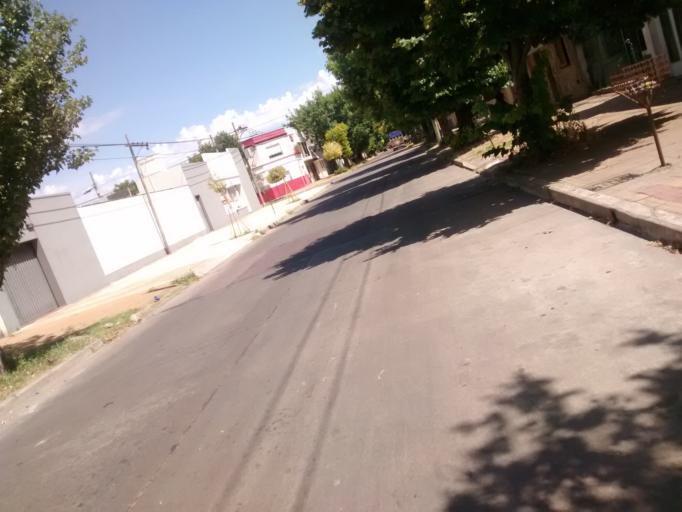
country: AR
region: Buenos Aires
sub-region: Partido de La Plata
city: La Plata
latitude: -34.8952
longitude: -57.9578
